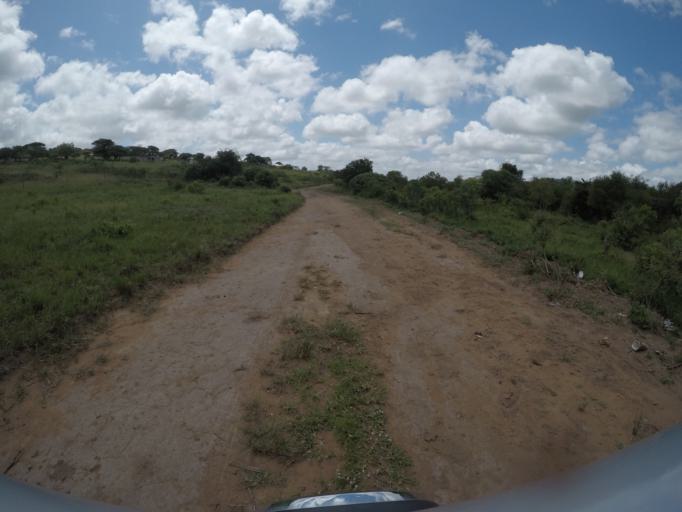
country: ZA
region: KwaZulu-Natal
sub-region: uThungulu District Municipality
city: Empangeni
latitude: -28.5891
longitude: 31.8394
